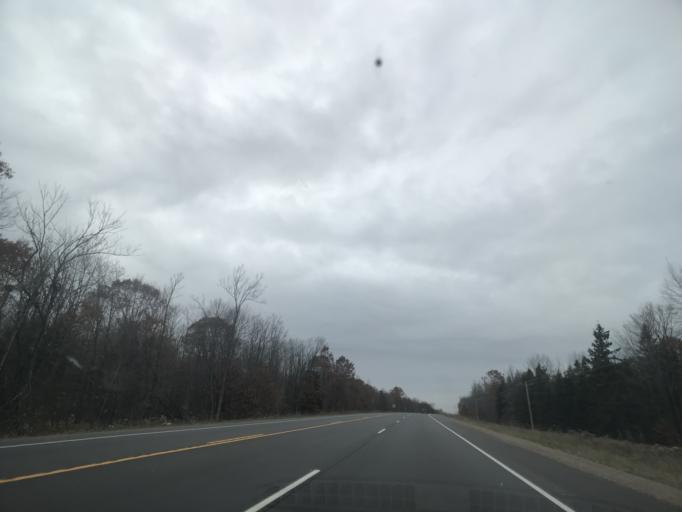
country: US
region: Wisconsin
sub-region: Menominee County
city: Legend Lake
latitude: 45.2224
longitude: -88.5144
